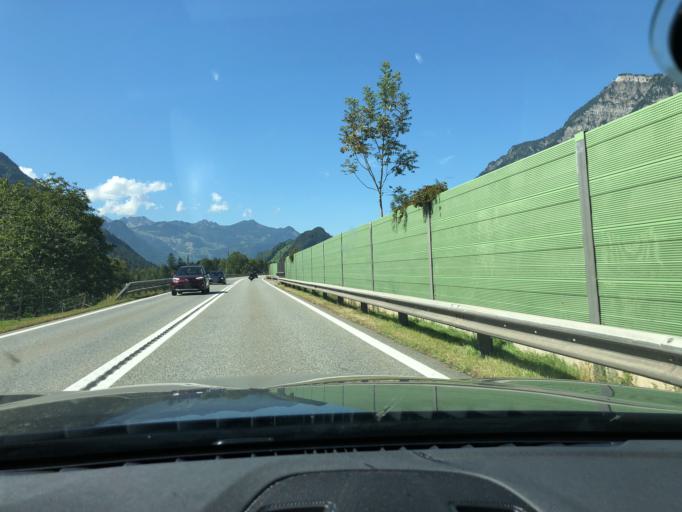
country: AT
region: Vorarlberg
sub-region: Politischer Bezirk Bludenz
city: Innerbraz
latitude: 47.1439
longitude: 9.9100
